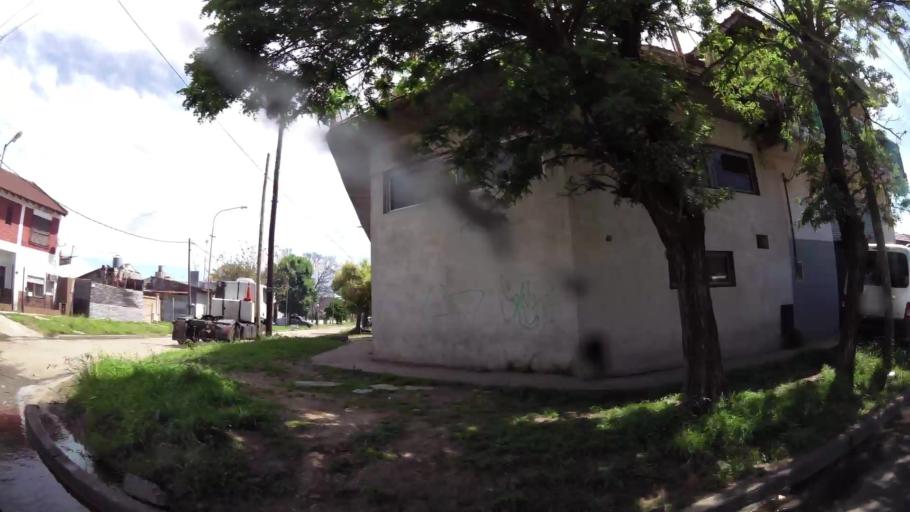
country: AR
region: Buenos Aires
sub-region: Partido de Quilmes
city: Quilmes
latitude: -34.7510
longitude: -58.2962
